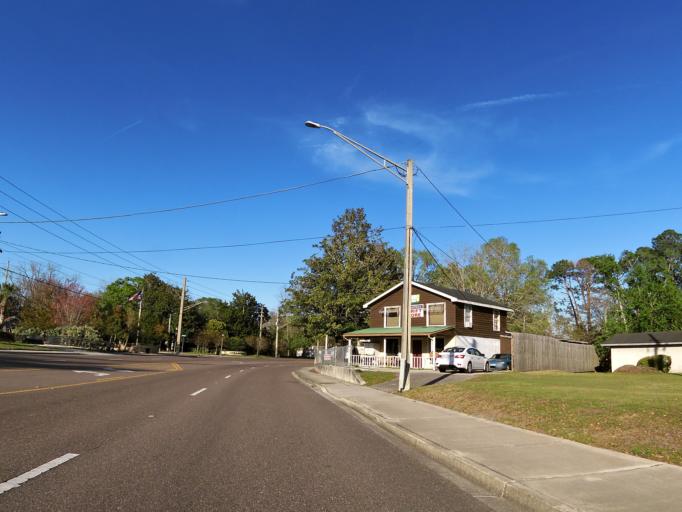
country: US
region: Florida
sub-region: Duval County
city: Jacksonville
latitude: 30.4656
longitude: -81.6282
